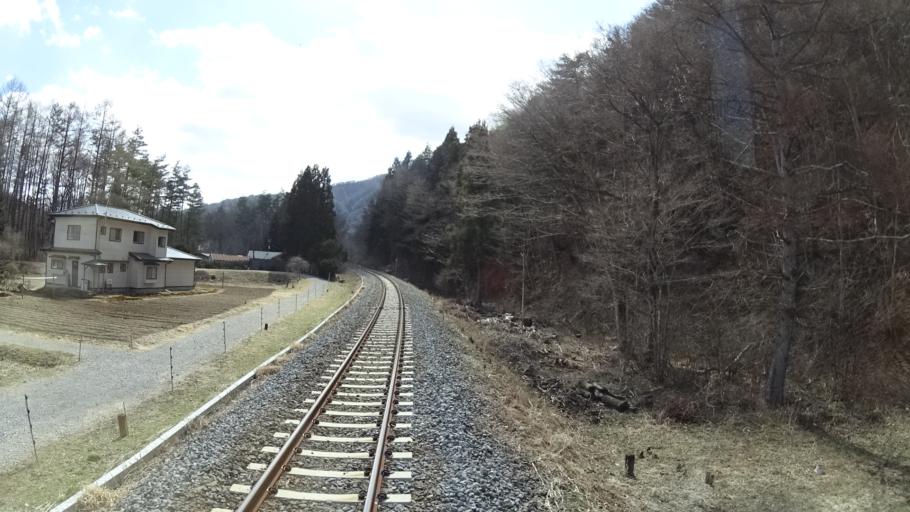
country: JP
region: Iwate
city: Yamada
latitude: 39.5180
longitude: 141.9157
